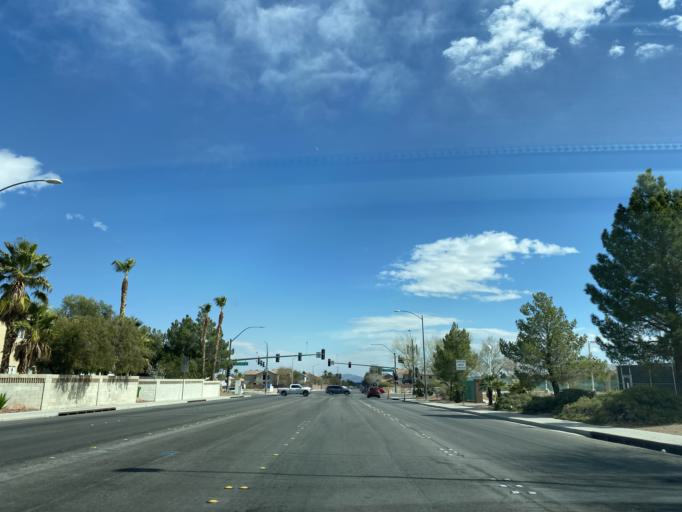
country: US
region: Nevada
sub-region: Clark County
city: Summerlin South
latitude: 36.2262
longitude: -115.2802
